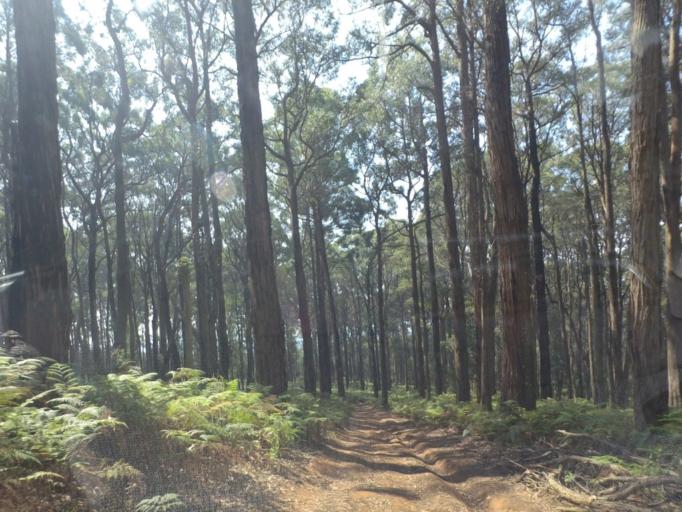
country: AU
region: Victoria
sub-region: Yarra Ranges
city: Healesville
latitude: -37.5606
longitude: 145.6349
